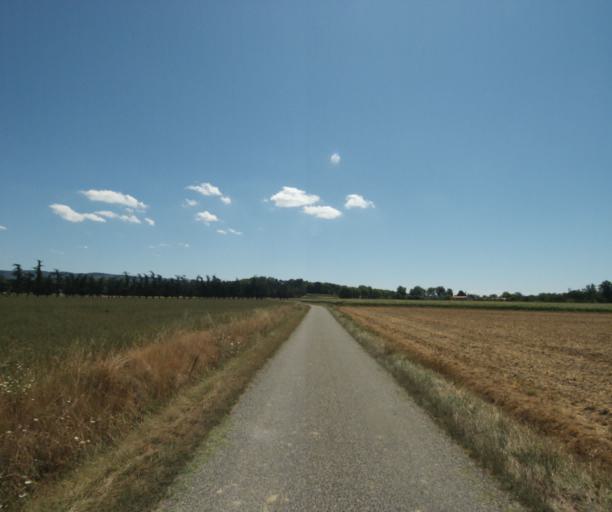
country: FR
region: Midi-Pyrenees
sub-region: Departement de la Haute-Garonne
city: Revel
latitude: 43.4501
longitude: 1.9490
